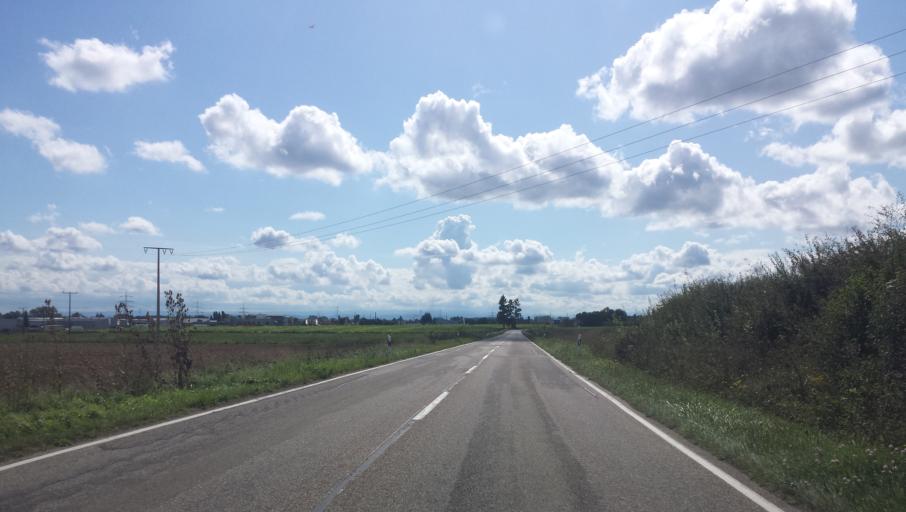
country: DE
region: Rheinland-Pfalz
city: Rulzheim
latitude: 49.1690
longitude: 8.2910
